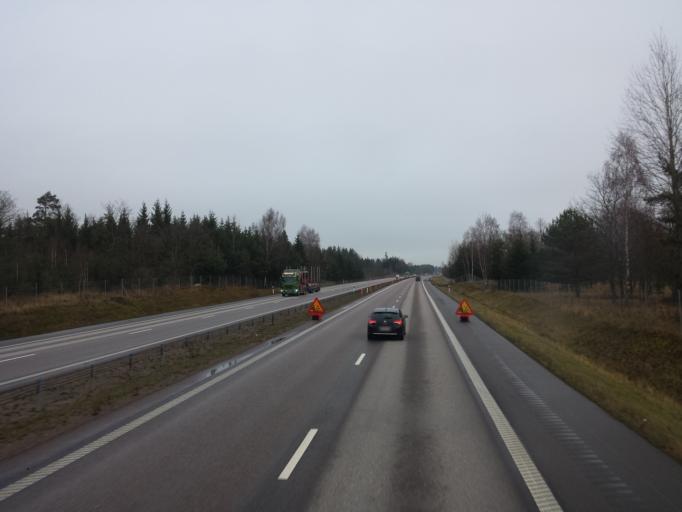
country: SE
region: OEstergoetland
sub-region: Linkopings Kommun
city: Linghem
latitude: 58.4628
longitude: 15.7958
